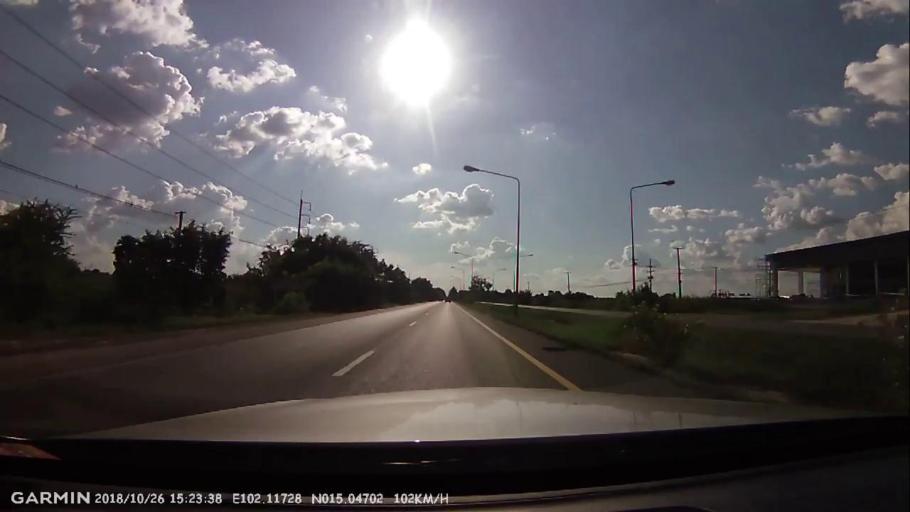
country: TH
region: Nakhon Ratchasima
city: Nakhon Ratchasima
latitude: 15.0471
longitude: 102.1174
